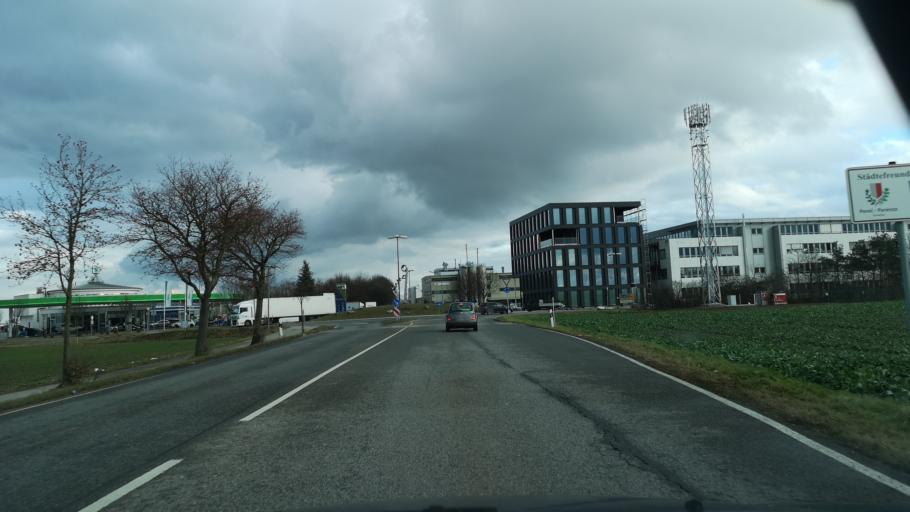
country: DE
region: Bavaria
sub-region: Upper Bavaria
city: Poing
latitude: 48.1680
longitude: 11.7906
